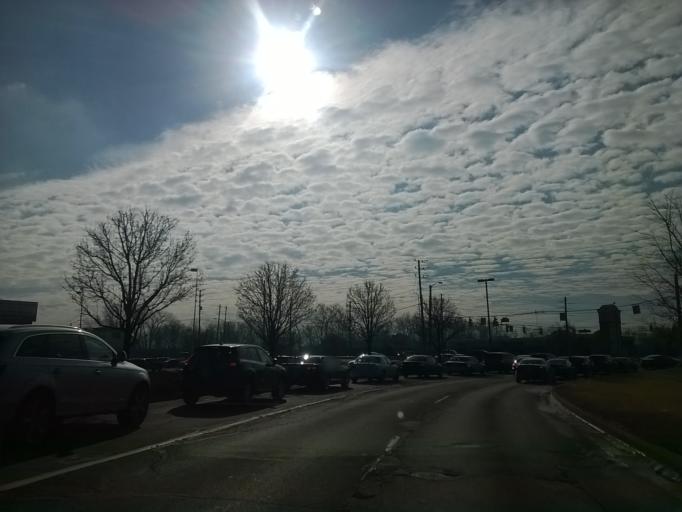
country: US
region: Indiana
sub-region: Marion County
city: Meridian Hills
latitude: 39.9117
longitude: -86.1065
